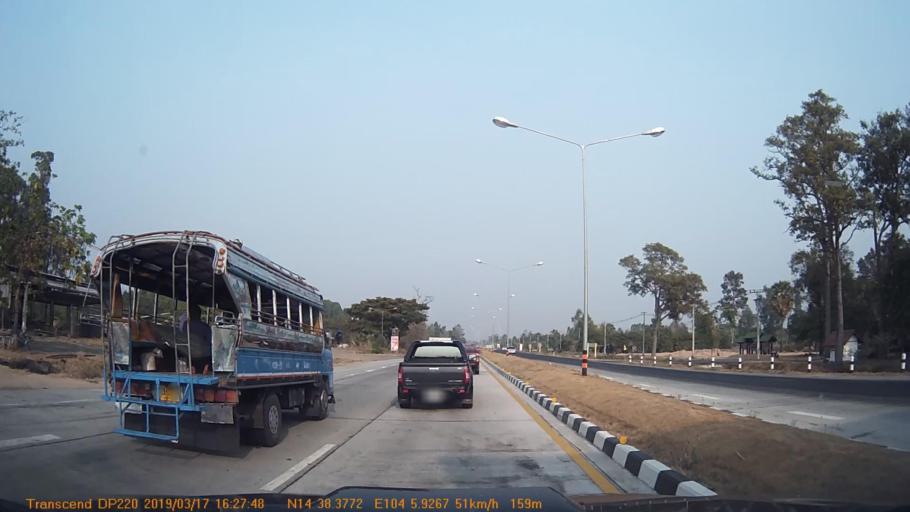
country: TH
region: Sisaket
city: Phu Sing
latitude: 14.6396
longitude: 104.0991
